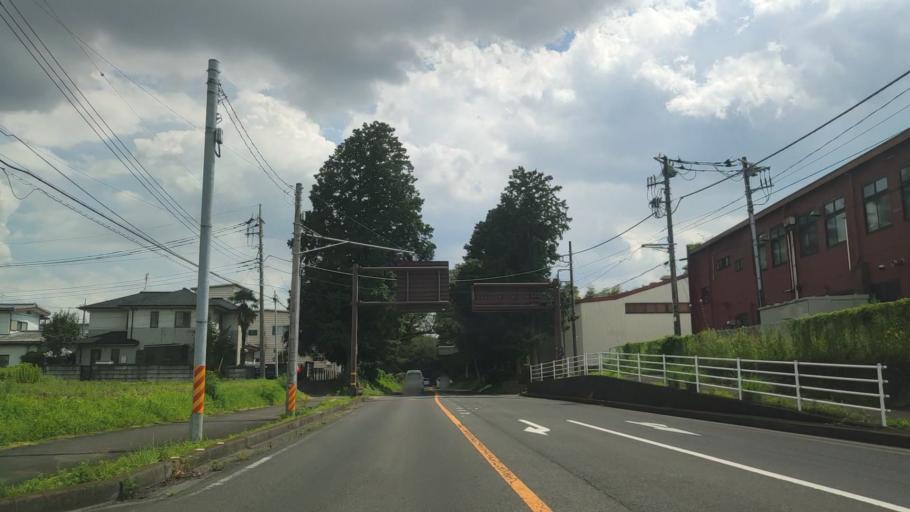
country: JP
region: Tochigi
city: Utsunomiya-shi
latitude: 36.6248
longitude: 139.8526
